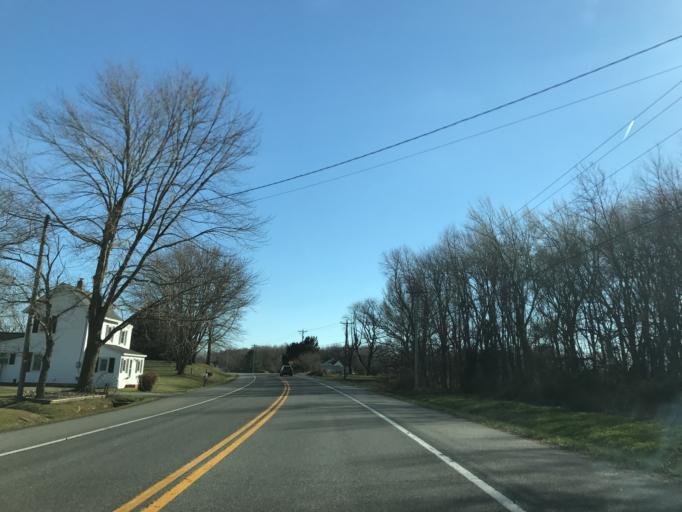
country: US
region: Maryland
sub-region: Caroline County
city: Greensboro
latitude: 39.1538
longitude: -75.8665
